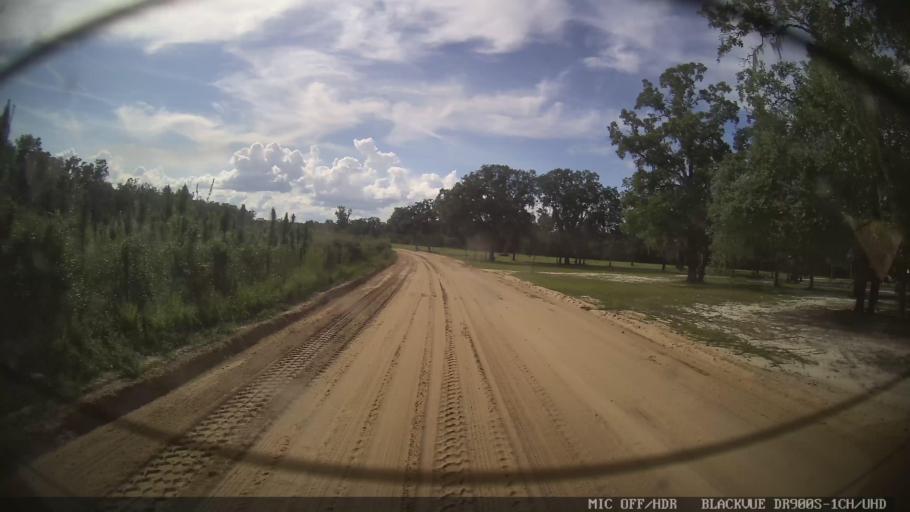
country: US
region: Georgia
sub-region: Echols County
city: Statenville
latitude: 30.6235
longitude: -83.1875
